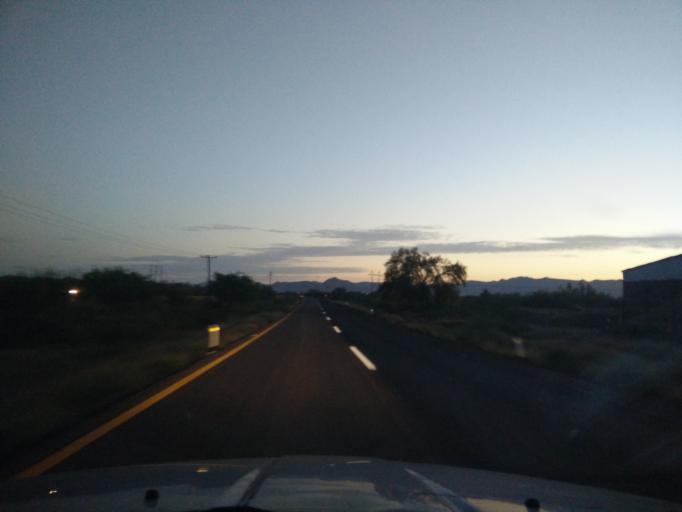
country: MX
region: Sonora
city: Heroica Guaymas
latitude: 28.0166
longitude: -110.9318
